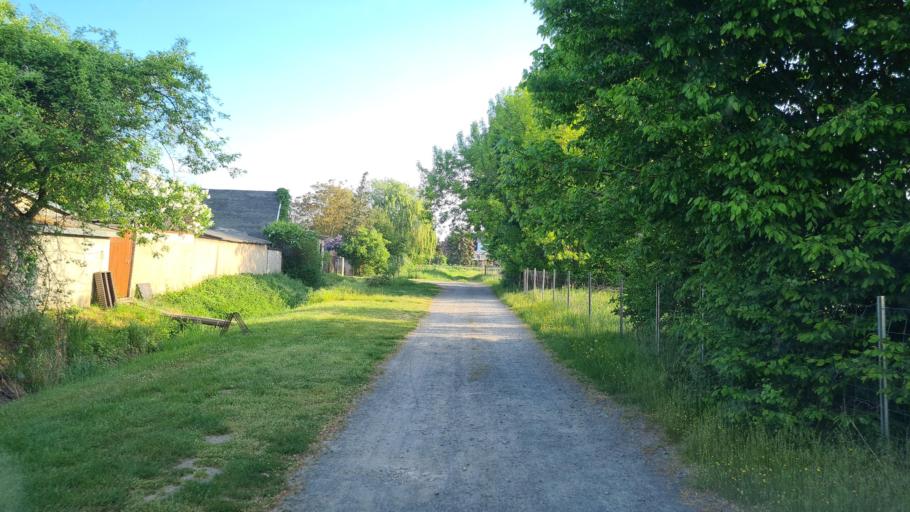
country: DE
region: Brandenburg
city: Falkenberg
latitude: 51.5834
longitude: 13.2276
